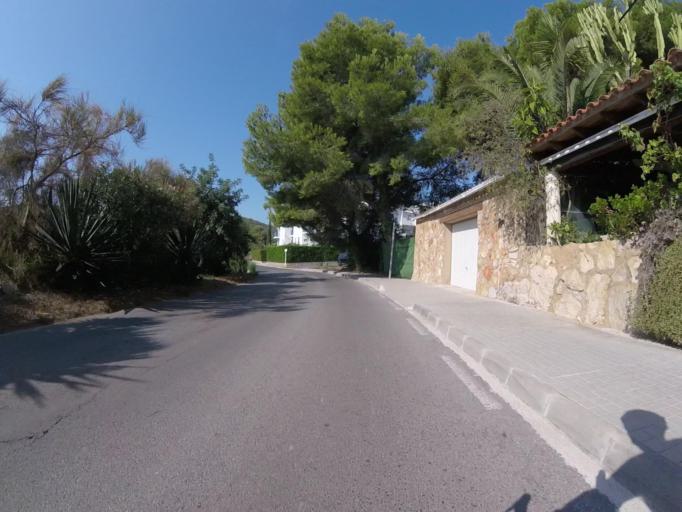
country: ES
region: Valencia
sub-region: Provincia de Castello
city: Peniscola
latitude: 40.3343
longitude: 0.3683
